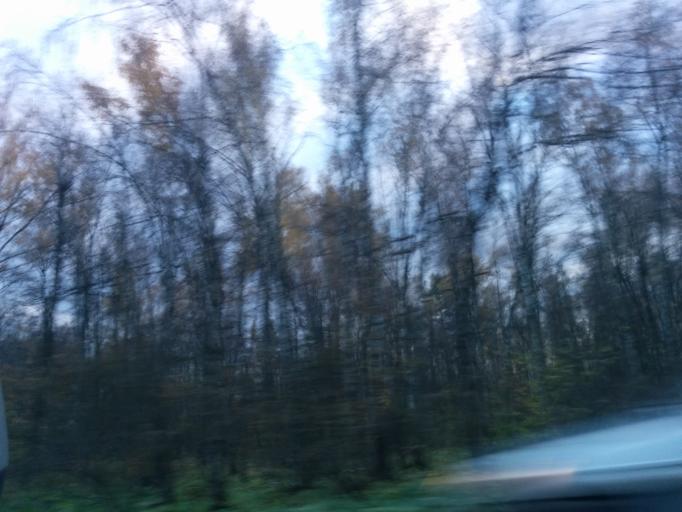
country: RU
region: Moskovskaya
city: Biryulevo Zapadnoye
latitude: 55.5421
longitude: 37.6258
